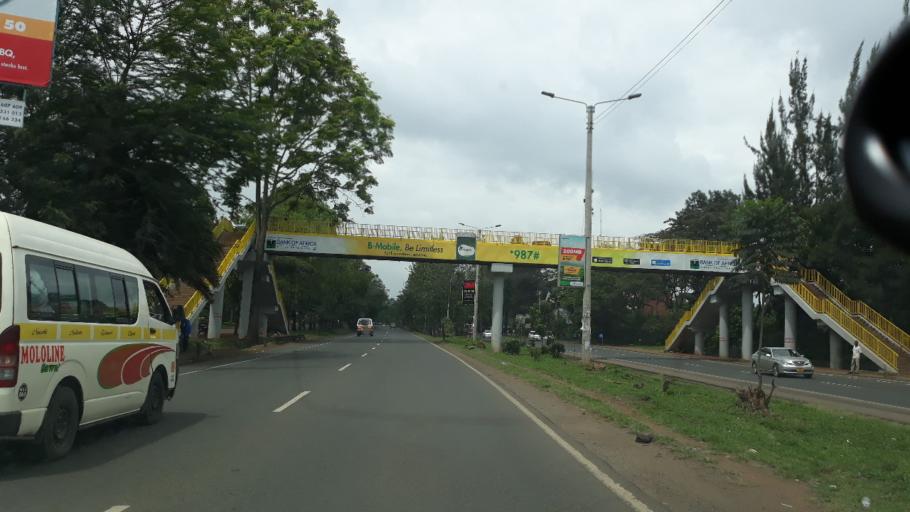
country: KE
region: Nairobi Area
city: Nairobi
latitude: -1.2612
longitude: 36.7974
